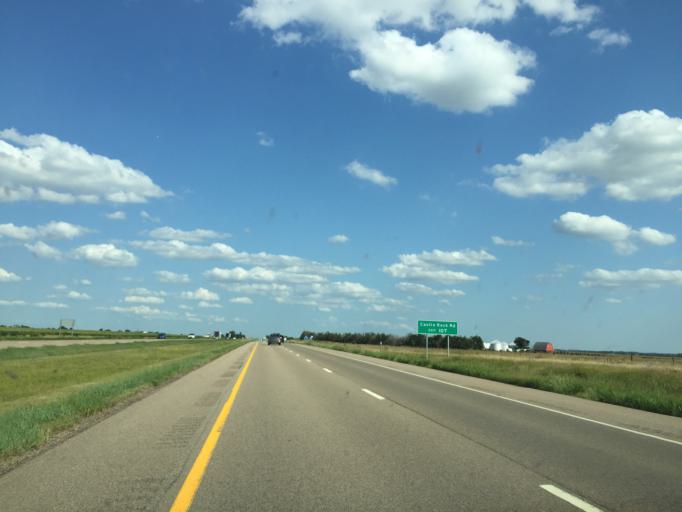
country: US
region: Kansas
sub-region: Gove County
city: Gove
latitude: 39.0645
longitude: -100.2557
